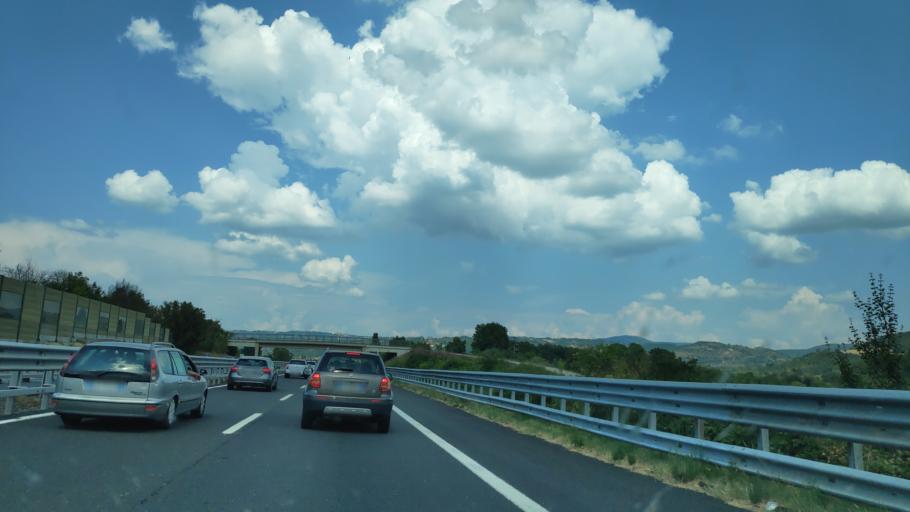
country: IT
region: Umbria
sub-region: Provincia di Terni
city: Fabro Scalo
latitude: 42.8547
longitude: 12.0378
